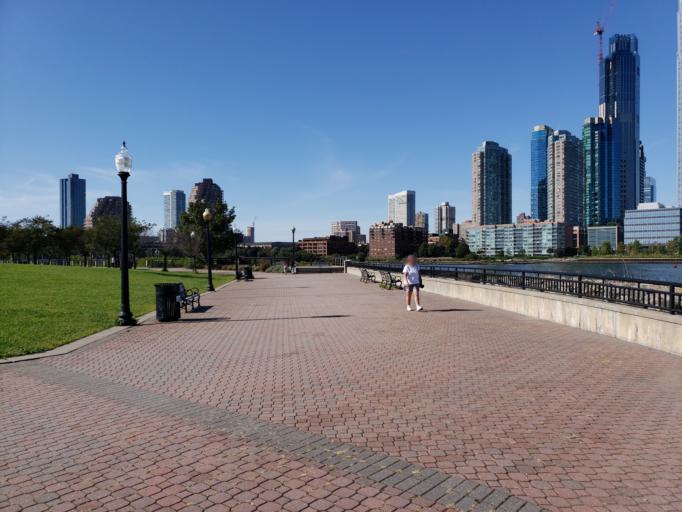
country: US
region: New York
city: New York City
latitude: 40.7085
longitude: -74.0343
